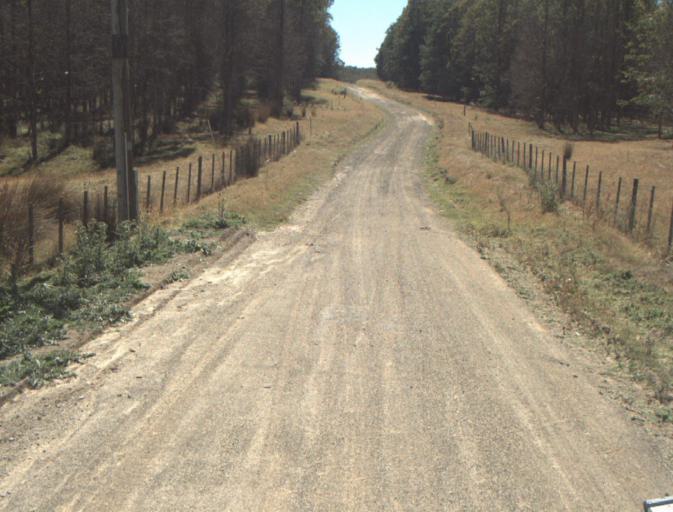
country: AU
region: Tasmania
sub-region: Dorset
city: Scottsdale
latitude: -41.2733
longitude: 147.3468
